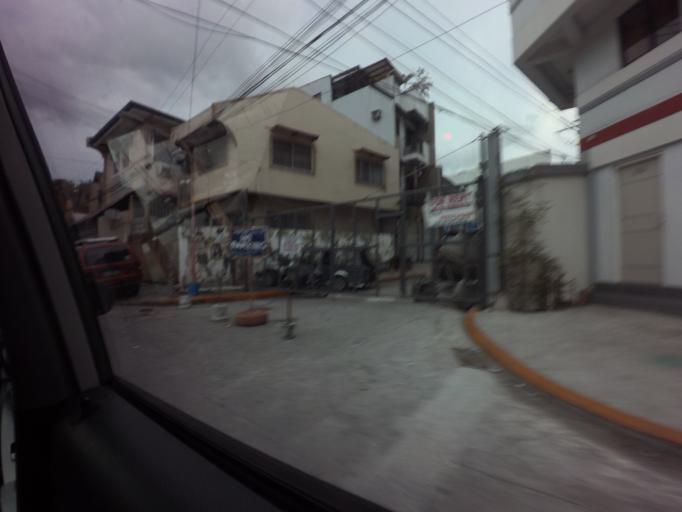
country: PH
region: Metro Manila
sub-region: City of Manila
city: Quiapo
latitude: 14.6064
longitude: 121.0077
